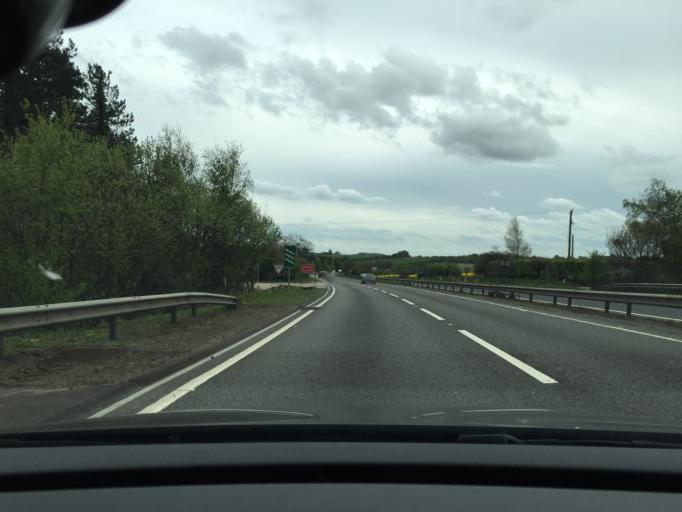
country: GB
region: England
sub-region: West Berkshire
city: Hermitage
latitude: 51.5046
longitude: -1.2940
